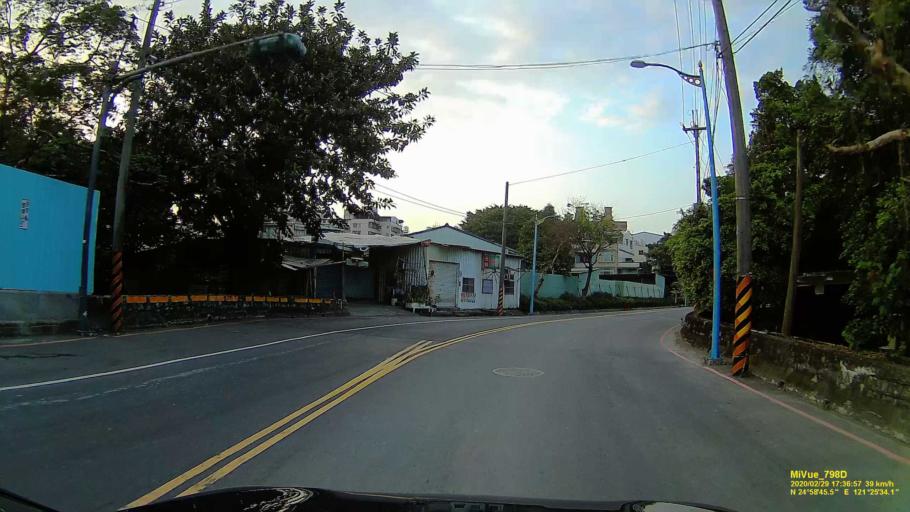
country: TW
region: Taipei
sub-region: Taipei
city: Banqiao
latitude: 24.9795
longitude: 121.4260
